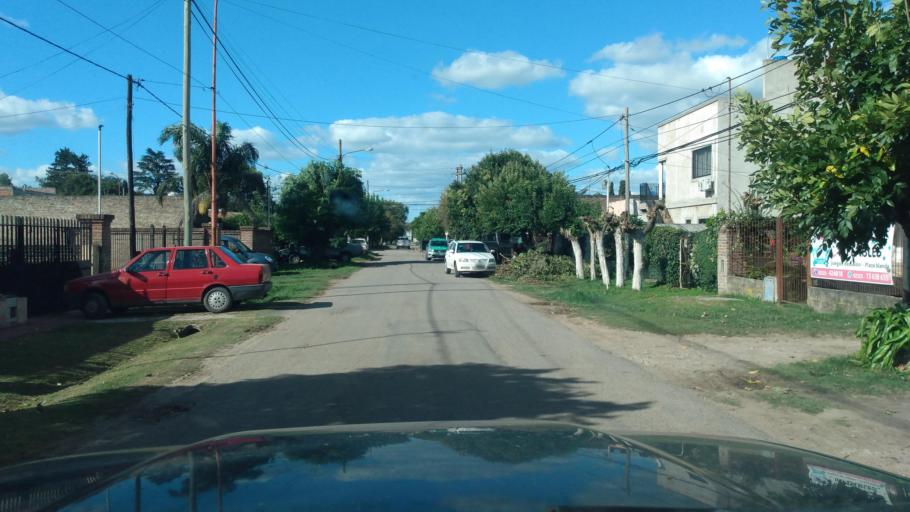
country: AR
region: Buenos Aires
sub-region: Partido de Lujan
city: Lujan
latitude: -34.5833
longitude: -59.0955
